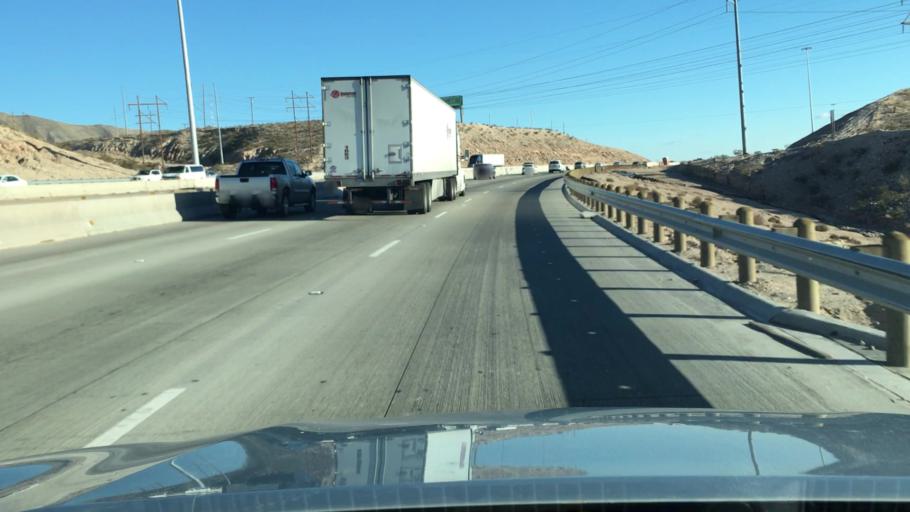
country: US
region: New Mexico
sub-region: Dona Ana County
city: Sunland Park
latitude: 31.8080
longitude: -106.5248
